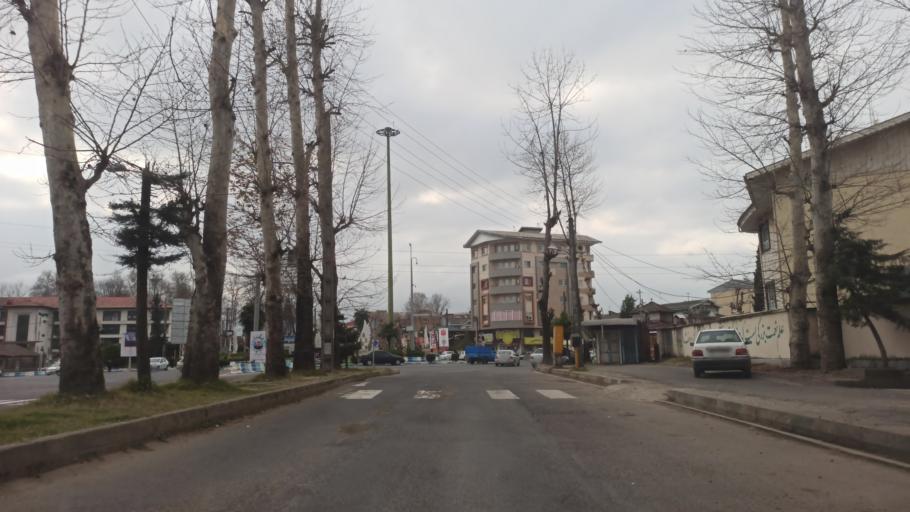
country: IR
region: Gilan
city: Fuman
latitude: 37.2332
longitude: 49.3196
